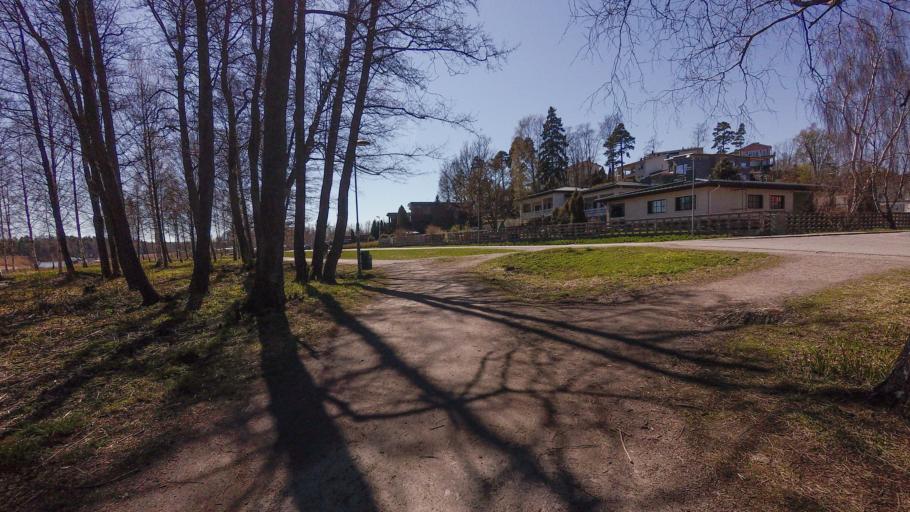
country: FI
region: Uusimaa
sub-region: Helsinki
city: Vantaa
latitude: 60.2180
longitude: 25.1193
